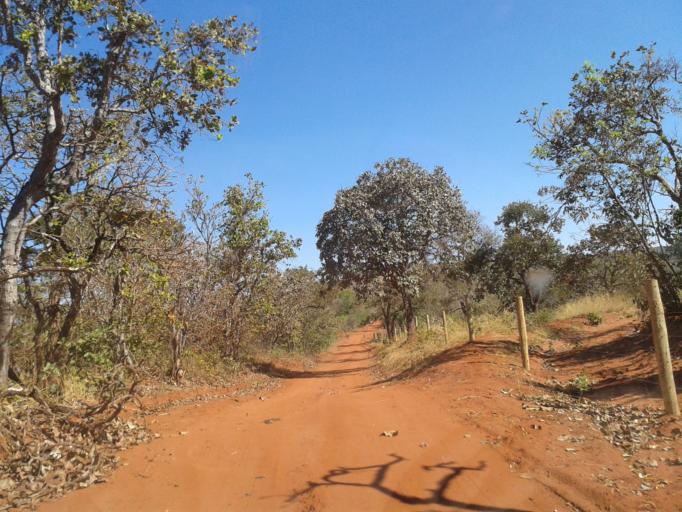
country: BR
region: Minas Gerais
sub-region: Ituiutaba
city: Ituiutaba
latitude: -19.0841
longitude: -49.3368
